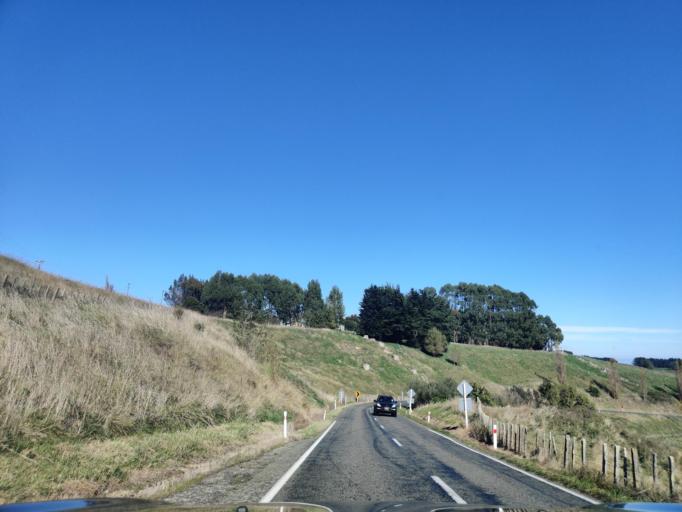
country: NZ
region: Manawatu-Wanganui
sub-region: Palmerston North City
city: Palmerston North
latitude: -40.2585
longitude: 175.7150
